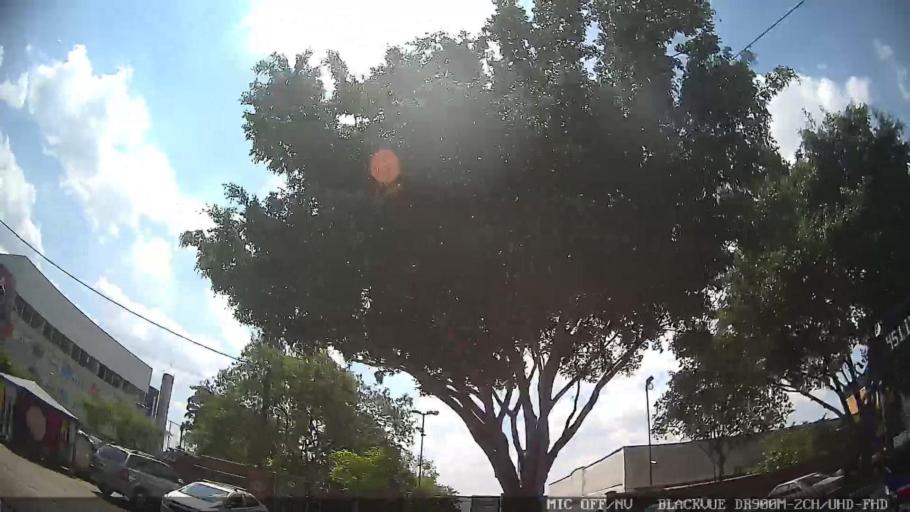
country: BR
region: Sao Paulo
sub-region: Taboao Da Serra
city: Taboao da Serra
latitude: -23.6770
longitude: -46.7932
